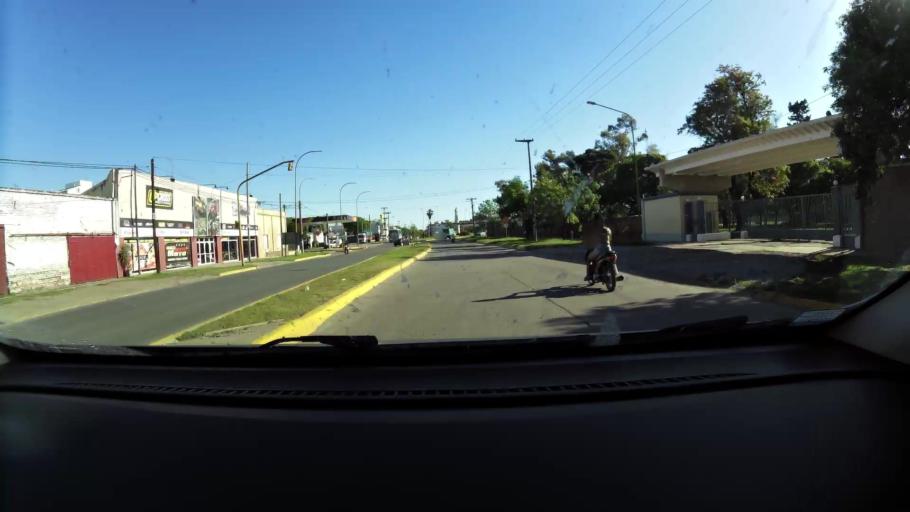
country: AR
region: Cordoba
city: San Francisco
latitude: -31.4269
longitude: -62.0968
